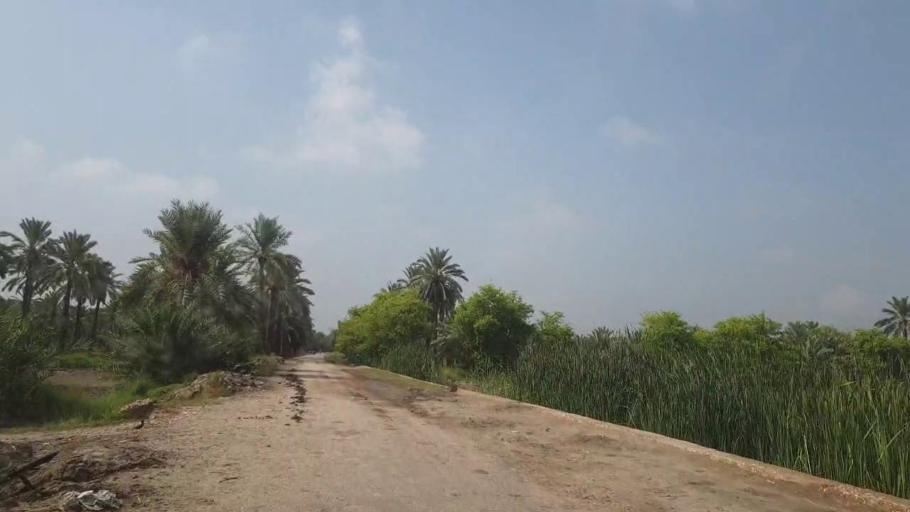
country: PK
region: Sindh
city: Khairpur
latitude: 27.5608
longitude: 68.7593
